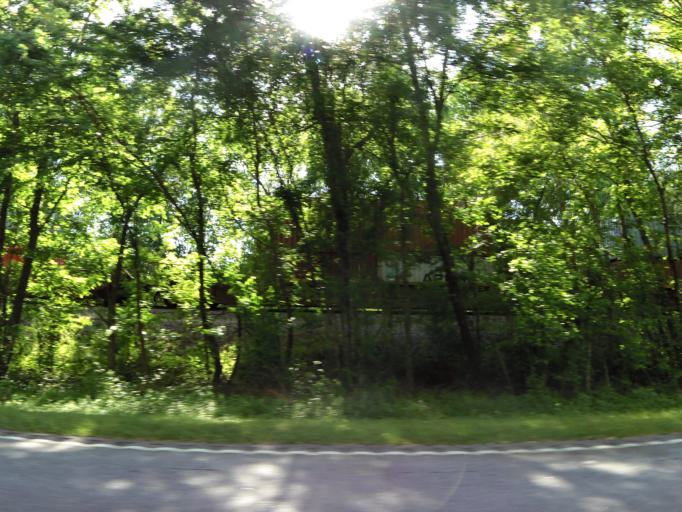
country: US
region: South Carolina
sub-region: Allendale County
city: Fairfax
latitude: 32.9003
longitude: -81.2379
